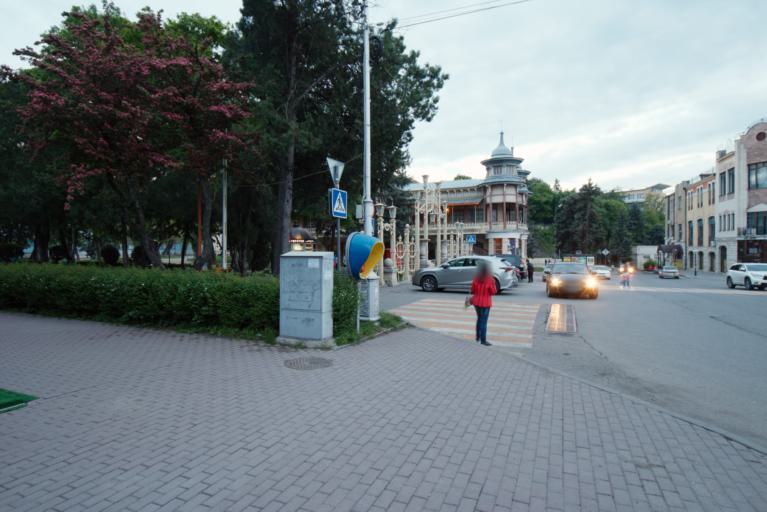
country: RU
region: Stavropol'skiy
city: Goryachevodskiy
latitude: 44.0371
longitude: 43.0799
